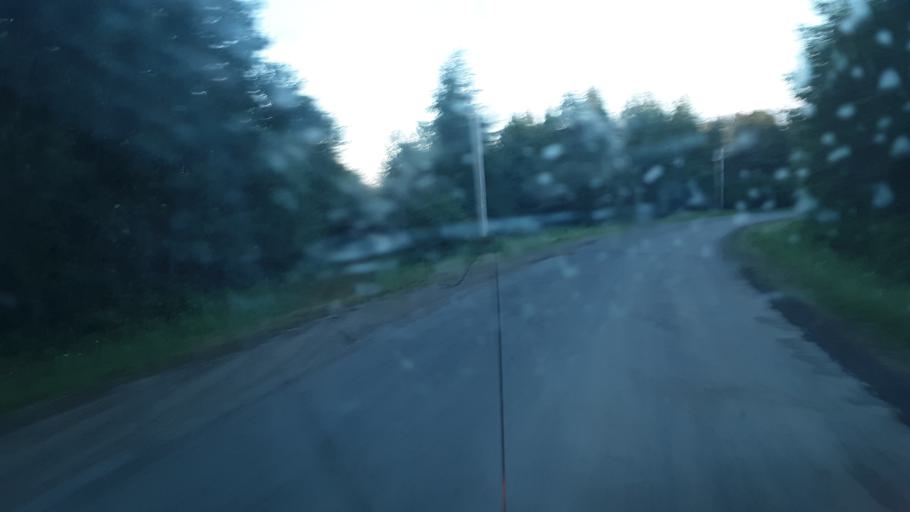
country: US
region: Maine
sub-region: Aroostook County
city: Caribou
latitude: 46.8487
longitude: -68.1346
